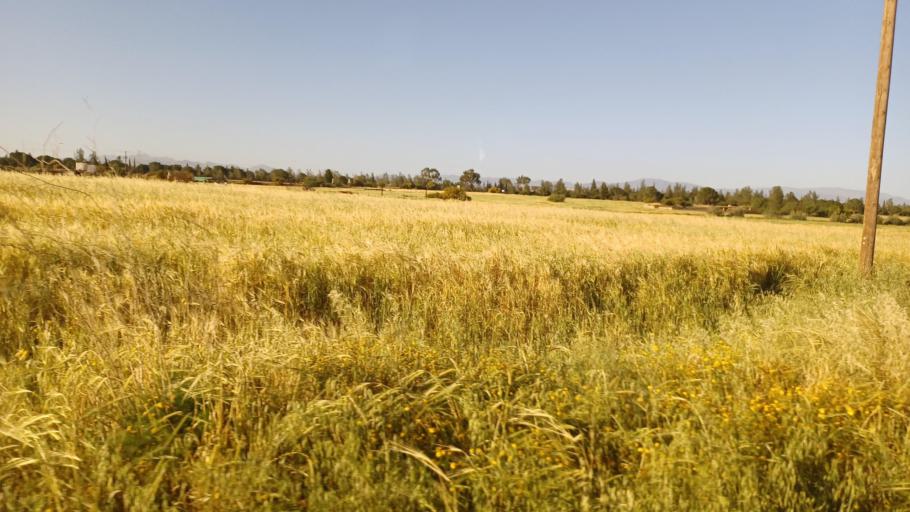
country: CY
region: Lefkosia
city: Kokkinotrimithia
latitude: 35.1499
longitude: 33.1776
